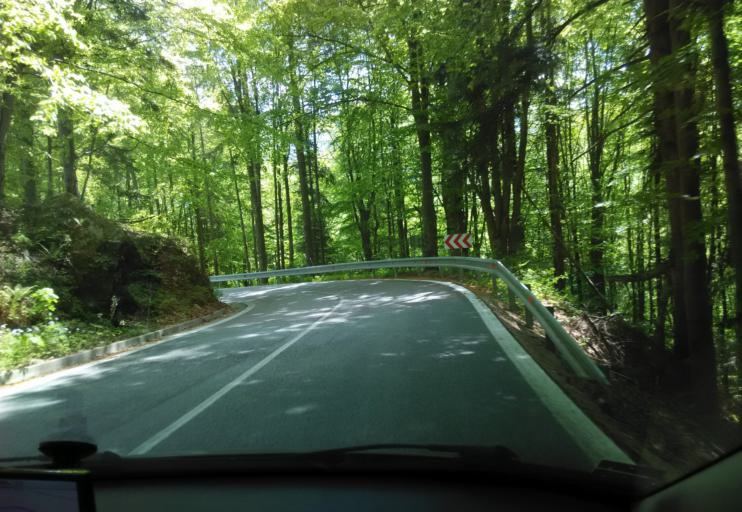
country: SK
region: Kosicky
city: Dobsina
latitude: 48.8504
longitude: 20.4600
